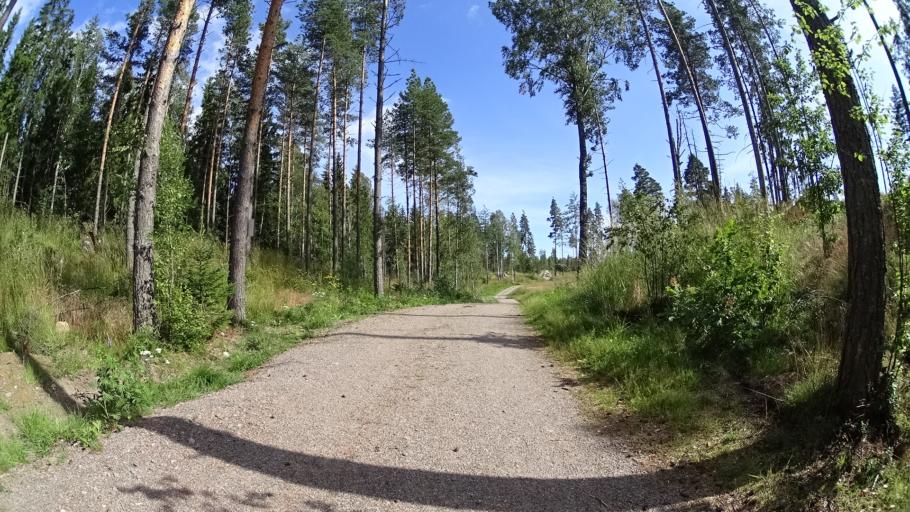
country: FI
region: Uusimaa
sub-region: Helsinki
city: Espoo
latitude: 60.2400
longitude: 24.6263
